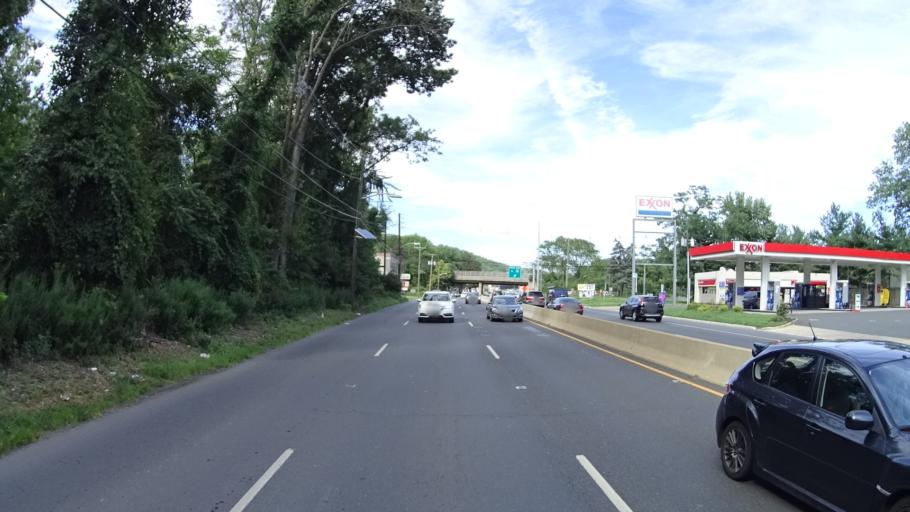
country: US
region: New Jersey
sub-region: Union County
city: Scotch Plains
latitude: 40.6523
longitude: -74.4049
